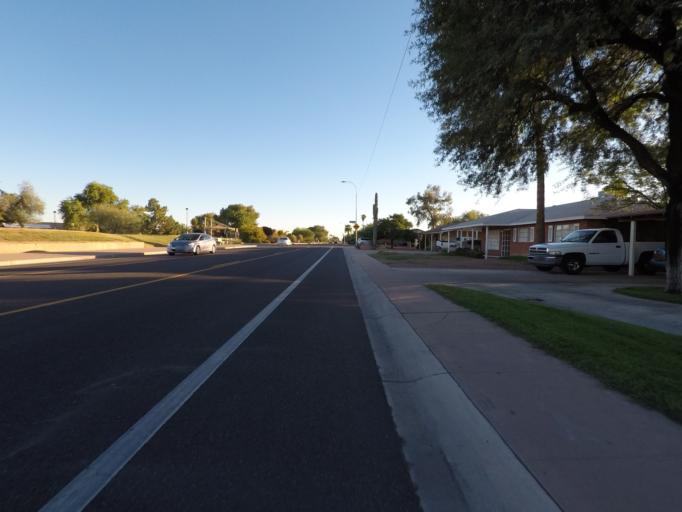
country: US
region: Arizona
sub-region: Maricopa County
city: Scottsdale
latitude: 33.4700
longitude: -111.9176
